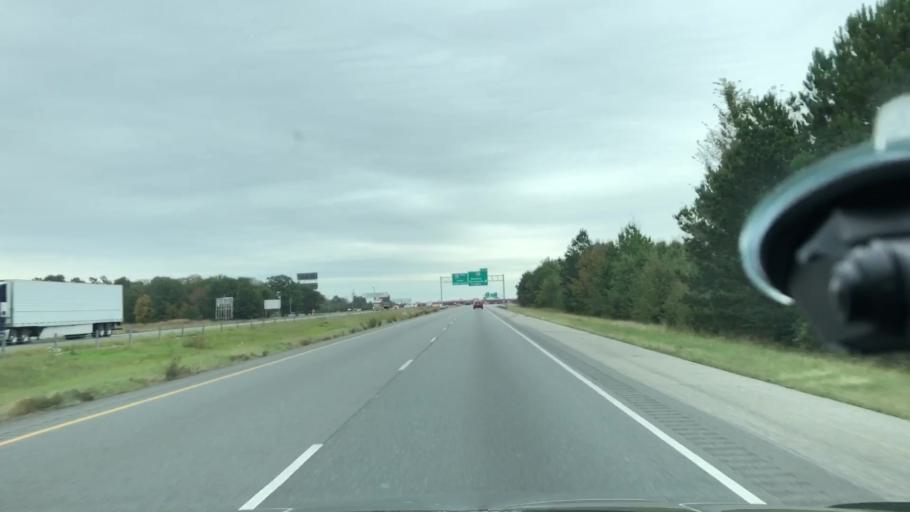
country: US
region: Arkansas
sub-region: Miller County
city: Texarkana
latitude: 33.4773
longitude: -93.9993
